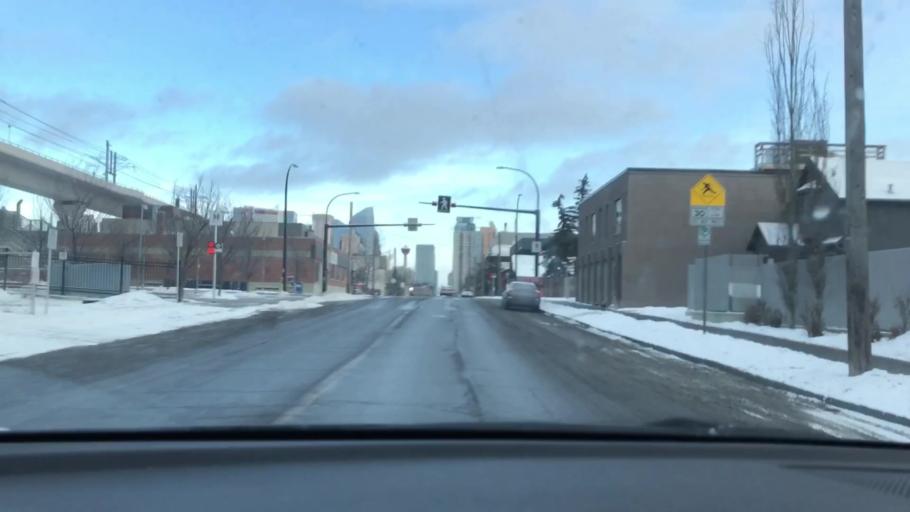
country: CA
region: Alberta
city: Calgary
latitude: 51.0444
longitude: -114.1001
